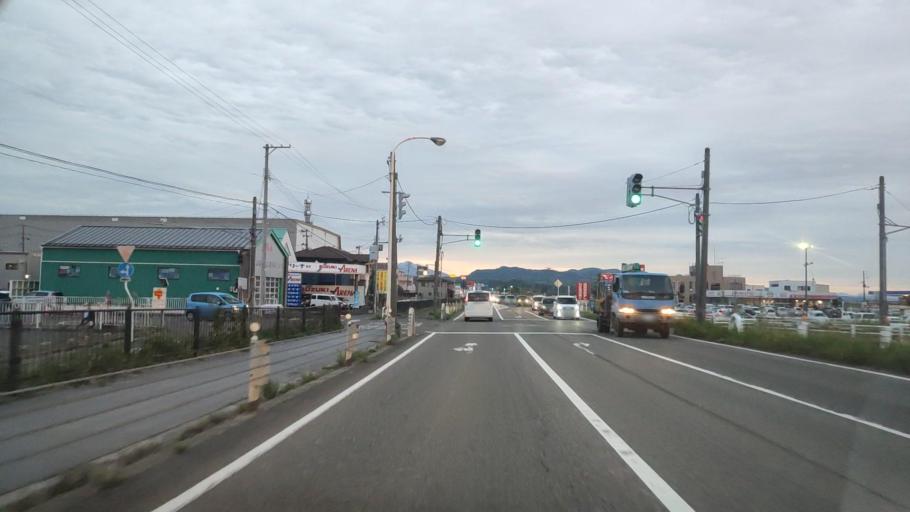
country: JP
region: Niigata
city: Niitsu-honcho
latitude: 37.7901
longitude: 139.1113
